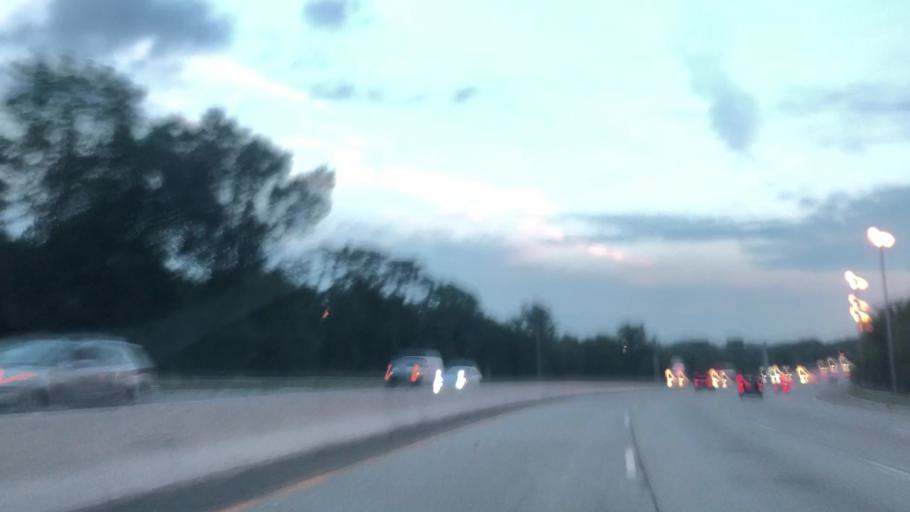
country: US
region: New Jersey
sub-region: Bergen County
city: Wallington
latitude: 40.8501
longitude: -74.1214
